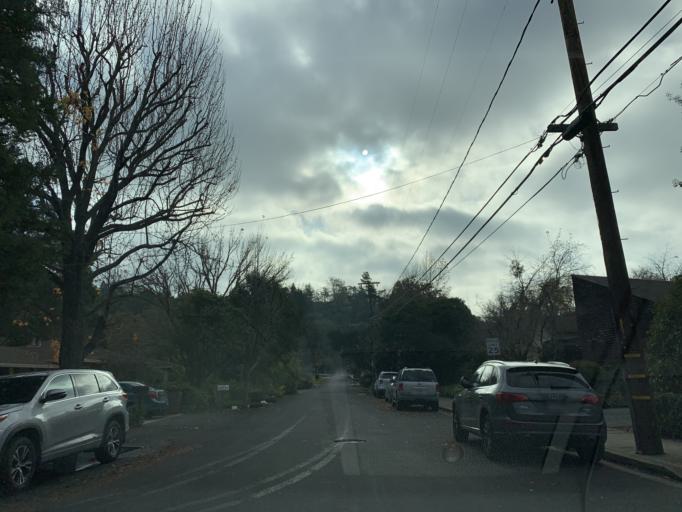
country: US
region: California
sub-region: Contra Costa County
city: Saranap
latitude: 37.8849
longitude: -122.0766
